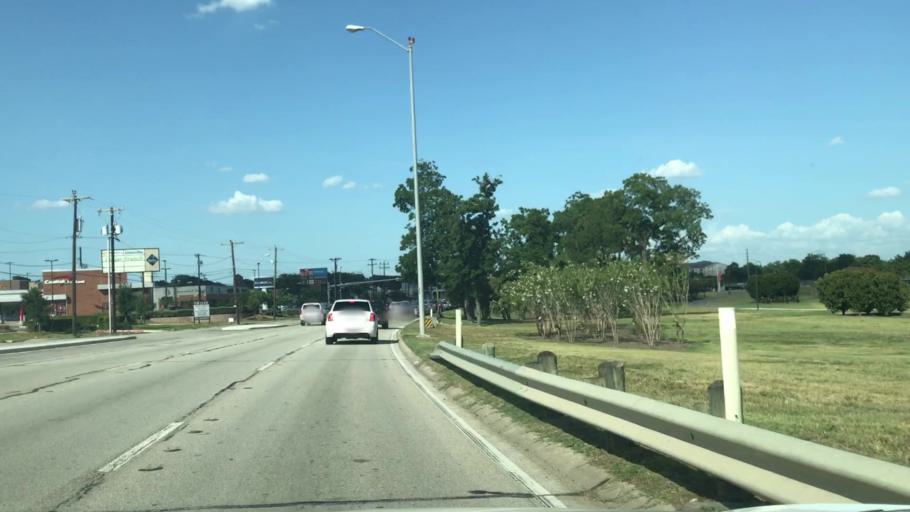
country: US
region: Texas
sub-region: Dallas County
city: University Park
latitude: 32.8597
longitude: -96.8595
